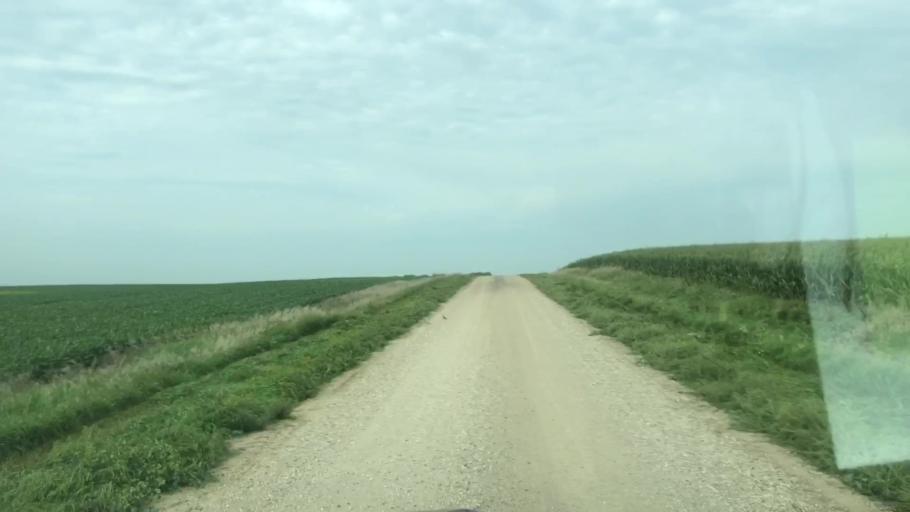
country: US
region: Iowa
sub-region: O'Brien County
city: Sheldon
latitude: 43.2720
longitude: -95.8639
